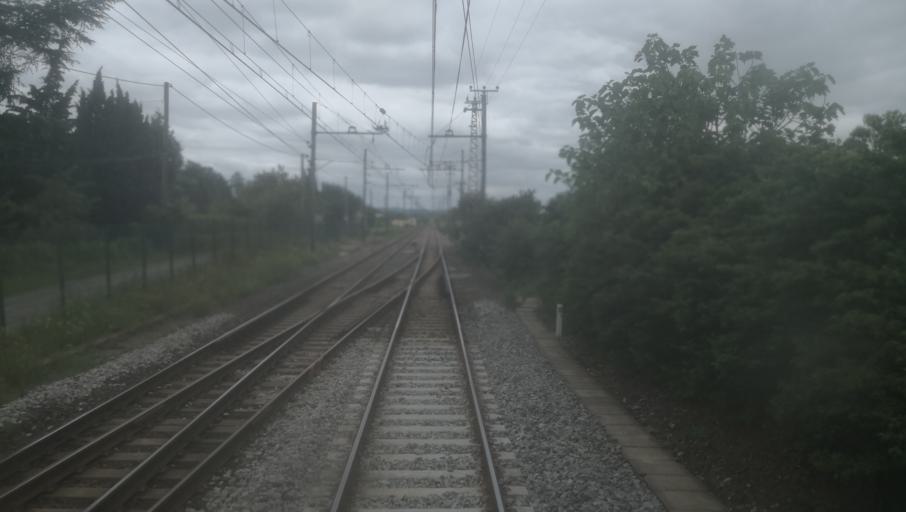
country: FR
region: Languedoc-Roussillon
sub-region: Departement de l'Aude
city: Castelnaudary
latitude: 43.3127
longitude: 1.9431
